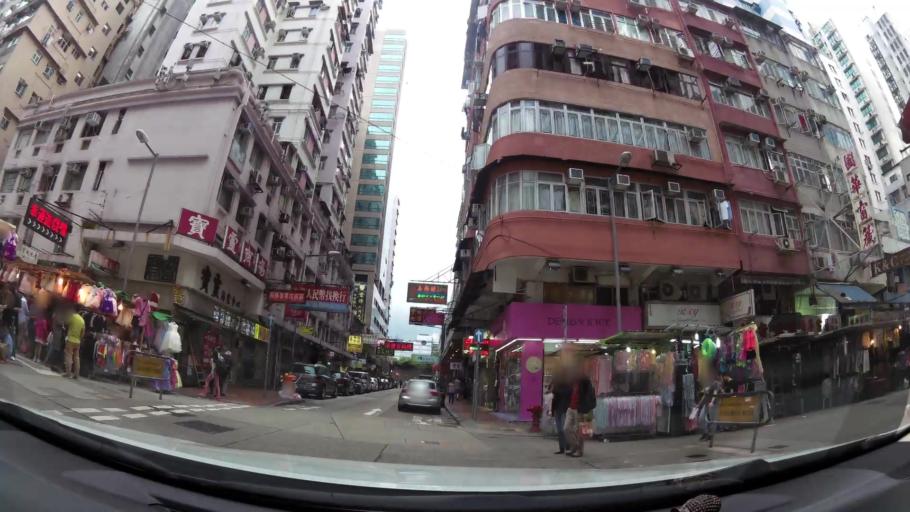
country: HK
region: Kowloon City
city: Kowloon
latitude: 22.3043
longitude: 114.1700
